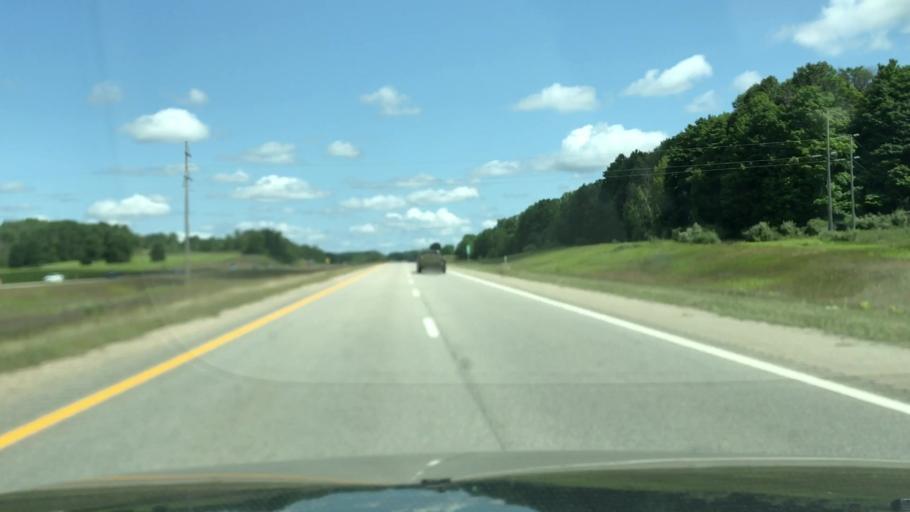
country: US
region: Michigan
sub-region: Osceola County
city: Reed City
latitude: 43.7893
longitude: -85.5342
